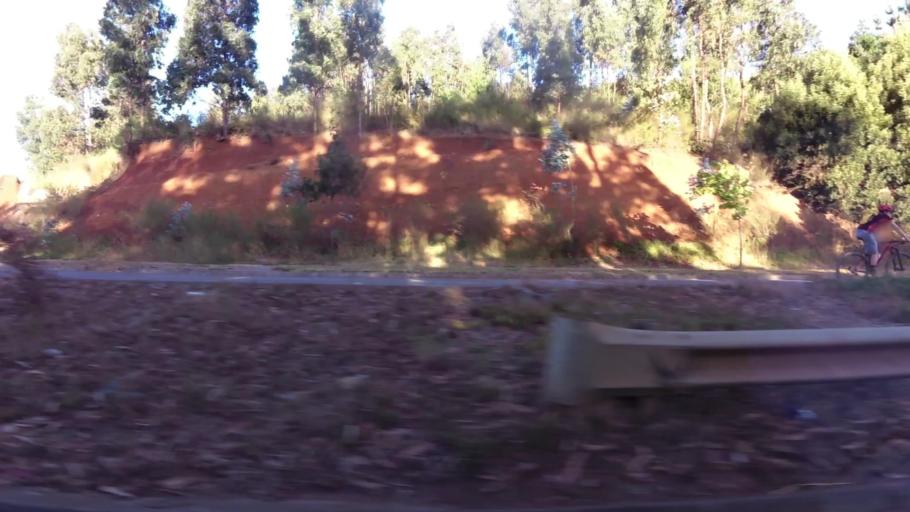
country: CL
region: Biobio
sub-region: Provincia de Concepcion
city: Concepcion
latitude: -36.8597
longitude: -73.0931
